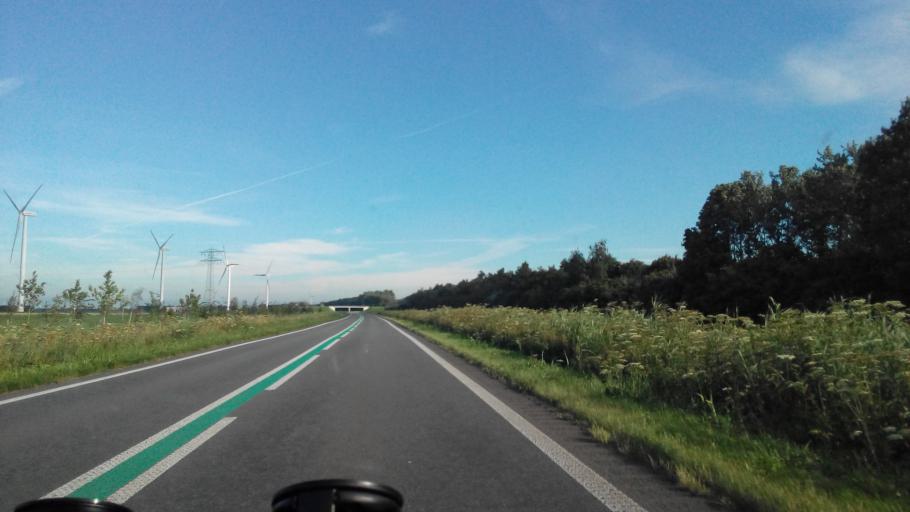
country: NL
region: Gelderland
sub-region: Gemeente Nijkerk
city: Nijkerk
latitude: 52.3056
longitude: 5.4491
